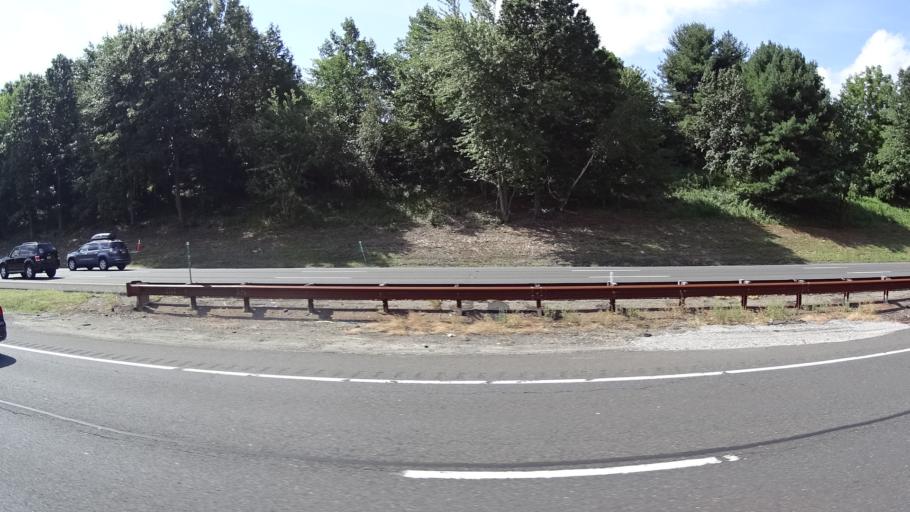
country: US
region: New Jersey
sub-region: Monmouth County
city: Matawan
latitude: 40.4282
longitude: -74.2288
